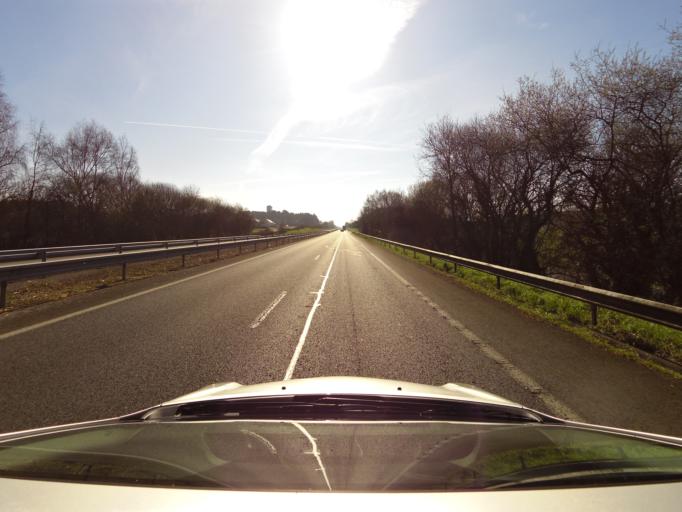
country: FR
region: Brittany
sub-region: Departement du Morbihan
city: Josselin
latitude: 47.9473
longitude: -2.5184
